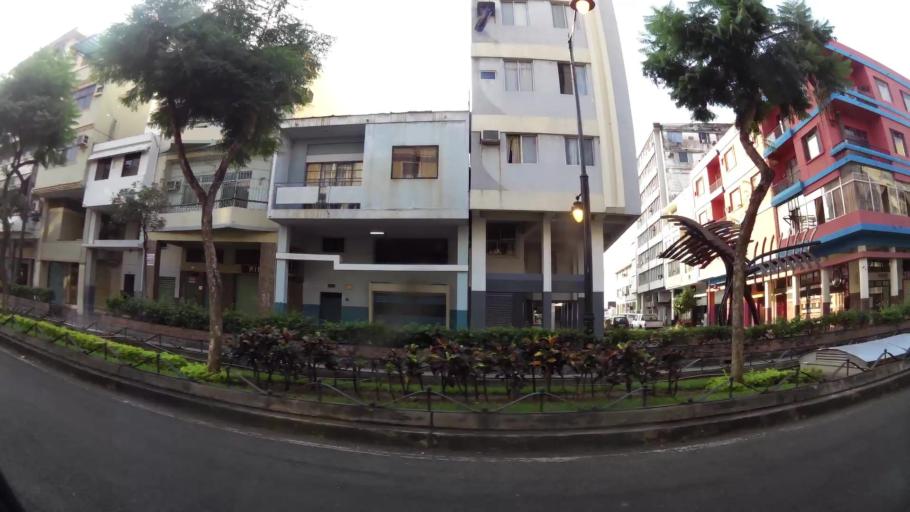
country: EC
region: Guayas
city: Eloy Alfaro
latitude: -2.1881
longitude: -79.8798
